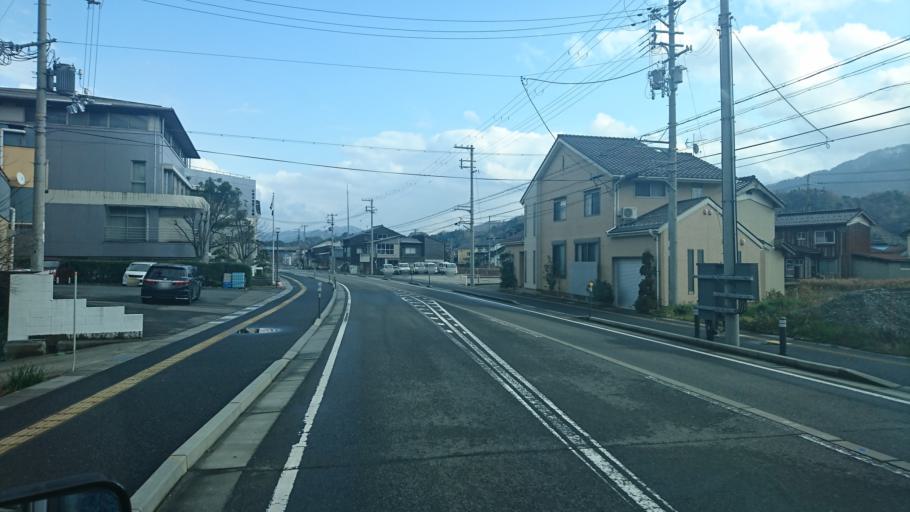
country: JP
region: Tottori
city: Tottori
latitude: 35.6230
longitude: 134.4469
